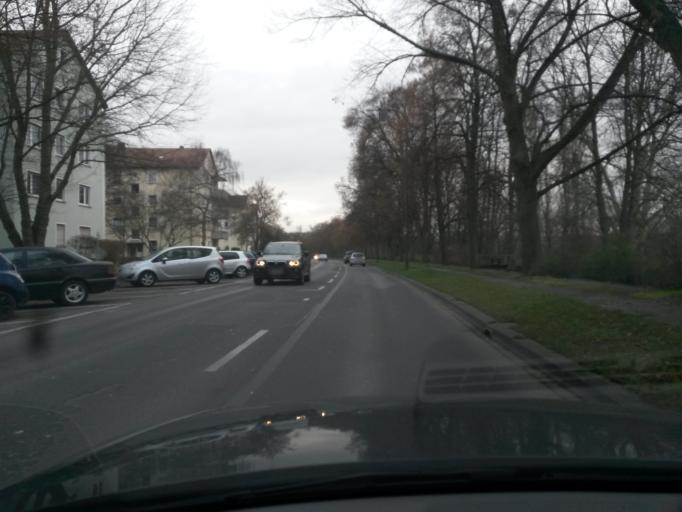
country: DE
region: Bavaria
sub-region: Regierungsbezirk Unterfranken
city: Wuerzburg
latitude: 49.7763
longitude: 9.9334
